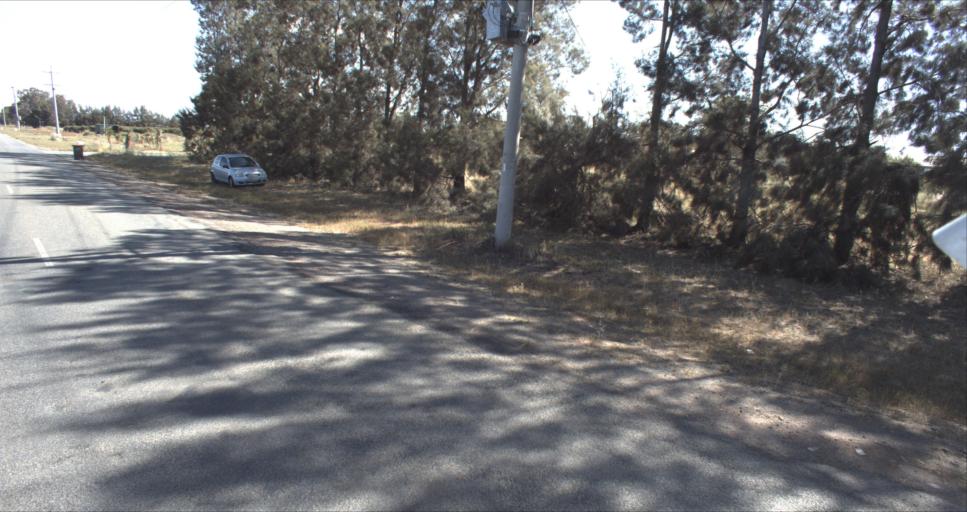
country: AU
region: New South Wales
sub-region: Leeton
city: Leeton
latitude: -34.5591
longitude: 146.3839
